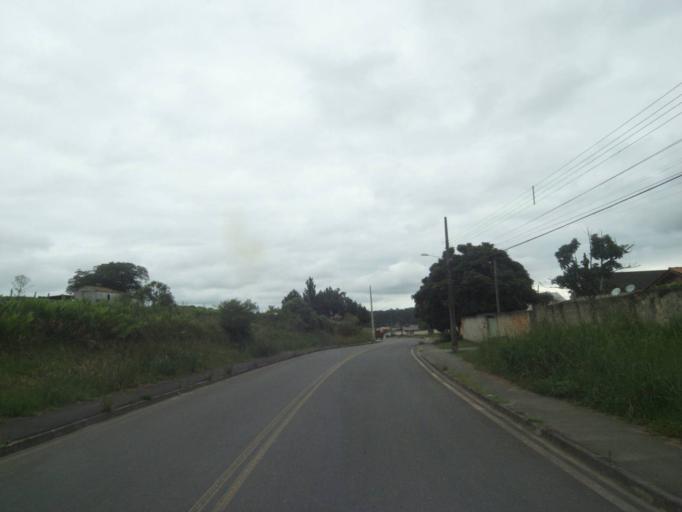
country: BR
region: Parana
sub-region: Quatro Barras
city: Quatro Barras
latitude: -25.3503
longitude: -49.1179
